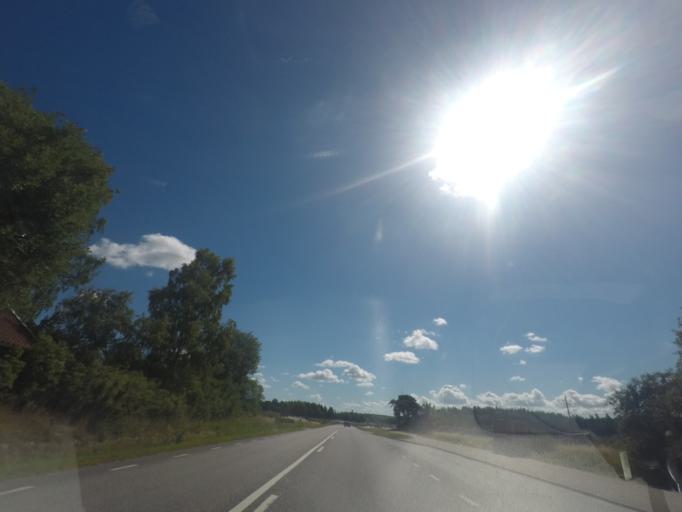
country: SE
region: Uppsala
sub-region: Uppsala Kommun
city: Saevja
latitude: 59.8574
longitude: 17.8161
